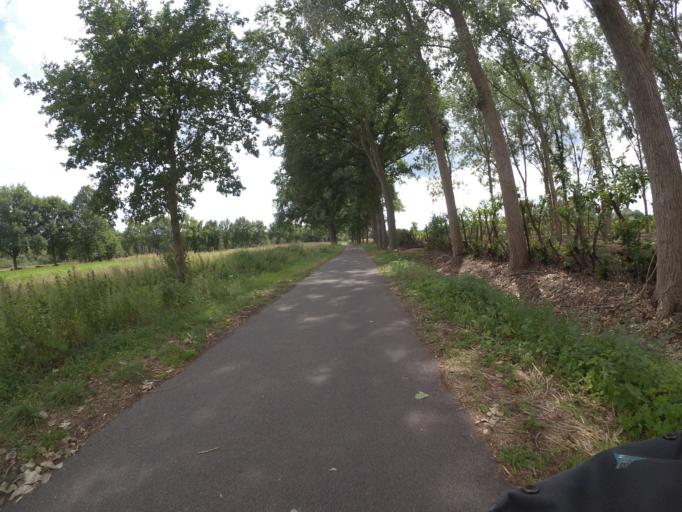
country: NL
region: North Brabant
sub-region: Gemeente Eindhoven
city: Muschberg en Geestenberg
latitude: 51.4431
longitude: 5.5342
